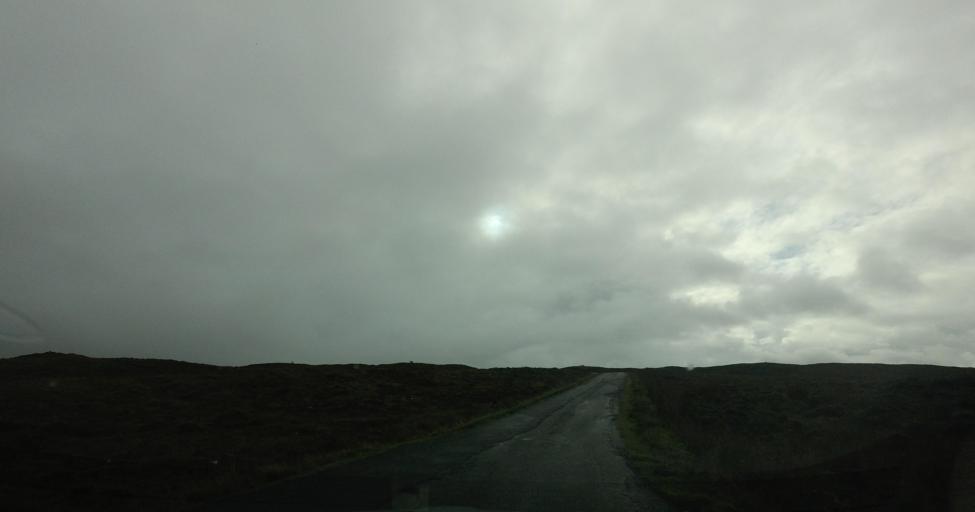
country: GB
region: Scotland
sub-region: Highland
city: Isle of Skye
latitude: 57.1458
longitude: -6.0924
